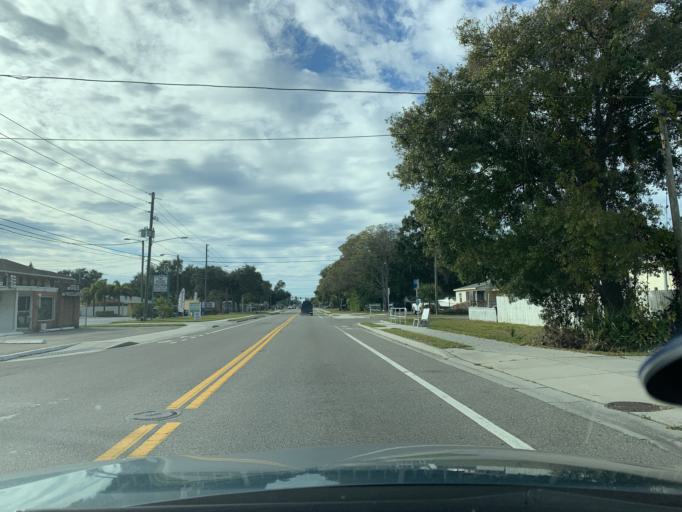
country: US
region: Florida
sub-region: Pinellas County
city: Kenneth City
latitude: 27.8137
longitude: -82.7333
